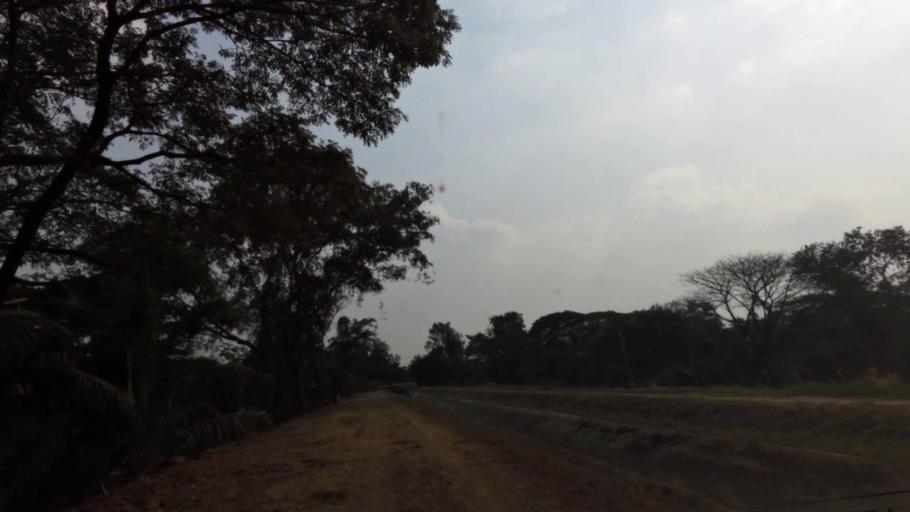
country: TH
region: Phra Nakhon Si Ayutthaya
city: Phra Nakhon Si Ayutthaya
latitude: 14.3117
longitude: 100.5629
